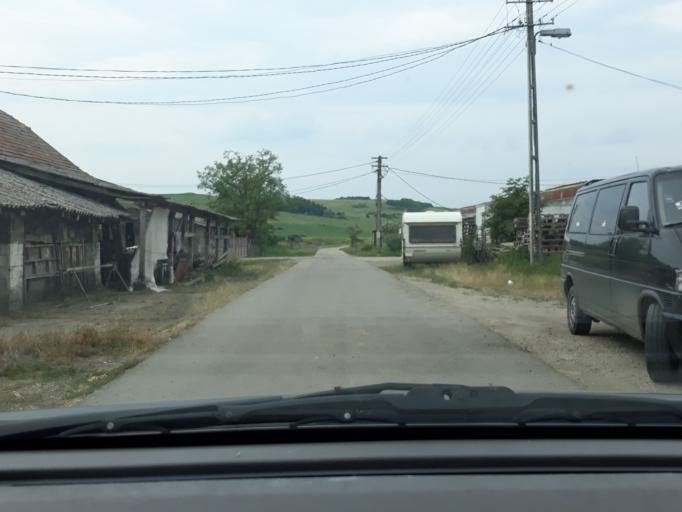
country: RO
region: Salaj
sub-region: Comuna Dobrin
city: Dobrin
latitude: 47.2876
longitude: 23.0951
